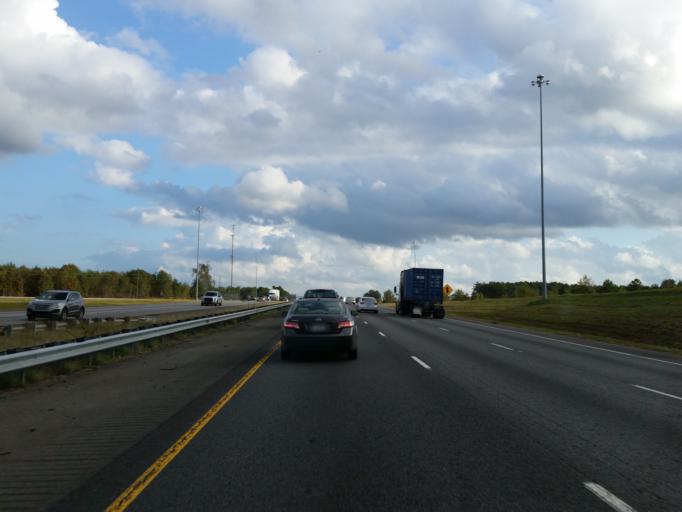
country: US
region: Georgia
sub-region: Henry County
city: Locust Grove
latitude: 33.2613
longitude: -84.0952
